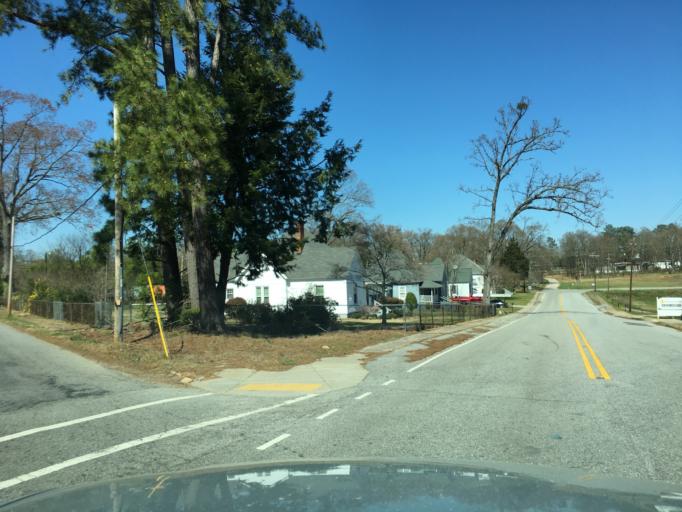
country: US
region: South Carolina
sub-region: Spartanburg County
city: Saxon
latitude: 34.9611
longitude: -81.9672
